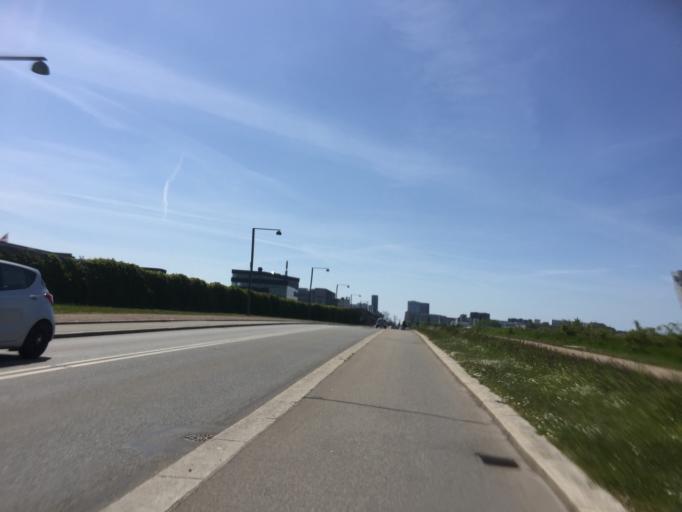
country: DK
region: Capital Region
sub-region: Tarnby Kommune
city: Tarnby
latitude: 55.6442
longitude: 12.5848
